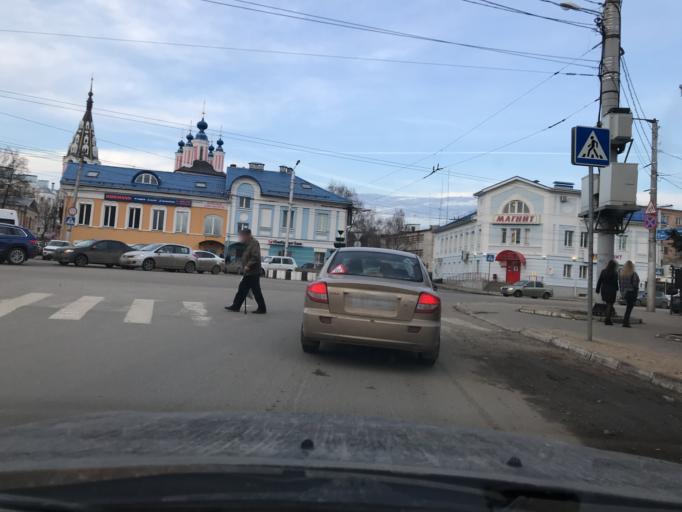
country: RU
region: Kaluga
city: Kaluga
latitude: 54.5121
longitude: 36.2423
